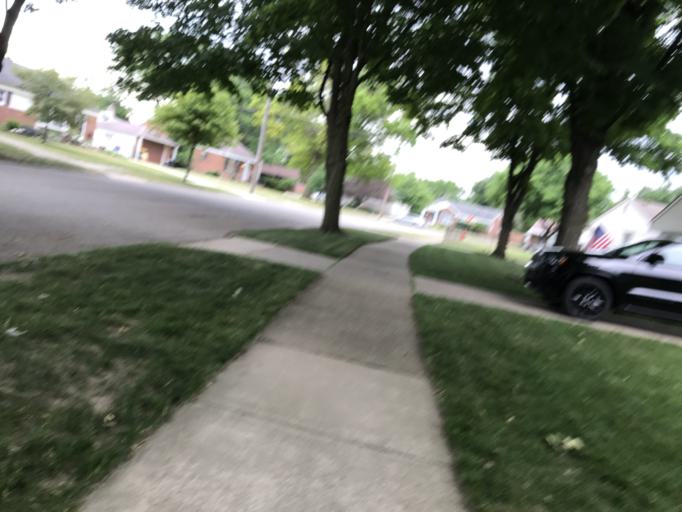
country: US
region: Michigan
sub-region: Oakland County
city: Farmington
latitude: 42.4687
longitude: -83.3608
